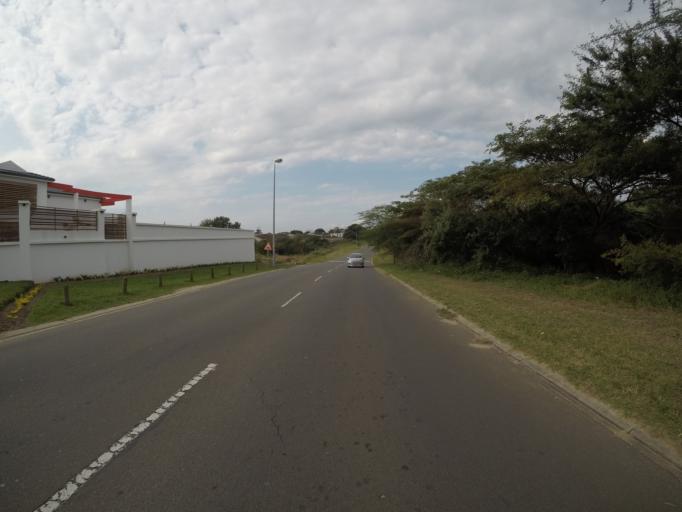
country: ZA
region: KwaZulu-Natal
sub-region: uThungulu District Municipality
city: Richards Bay
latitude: -28.7363
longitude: 32.0862
